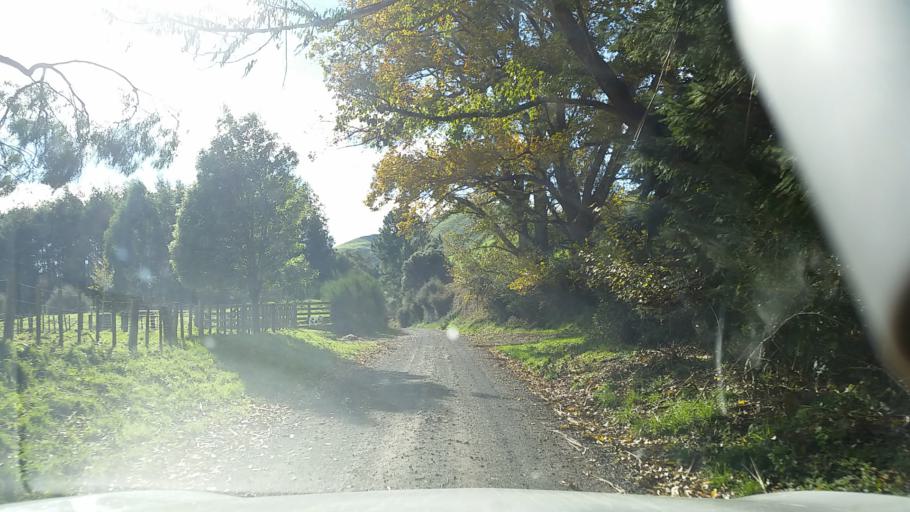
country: NZ
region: Bay of Plenty
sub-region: Rotorua District
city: Rotorua
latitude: -38.3850
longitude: 176.1994
